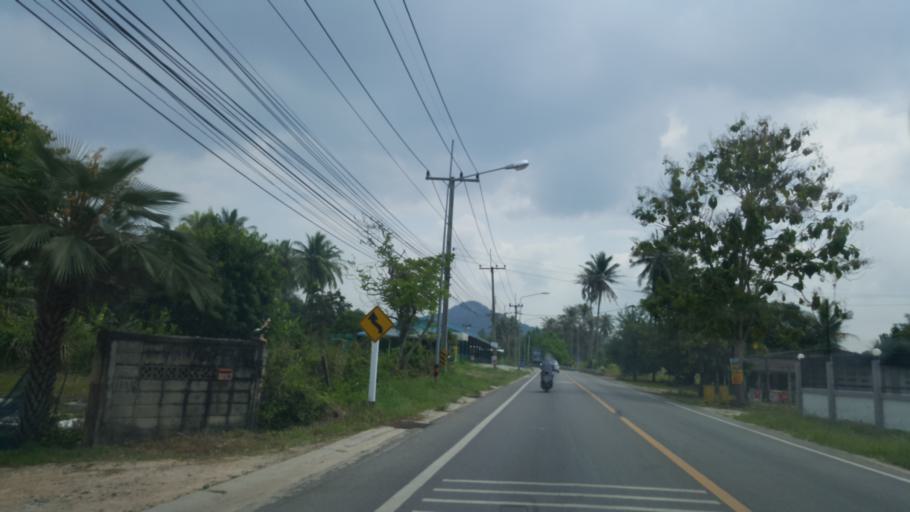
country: TH
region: Chon Buri
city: Si Racha
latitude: 13.2100
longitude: 101.0279
